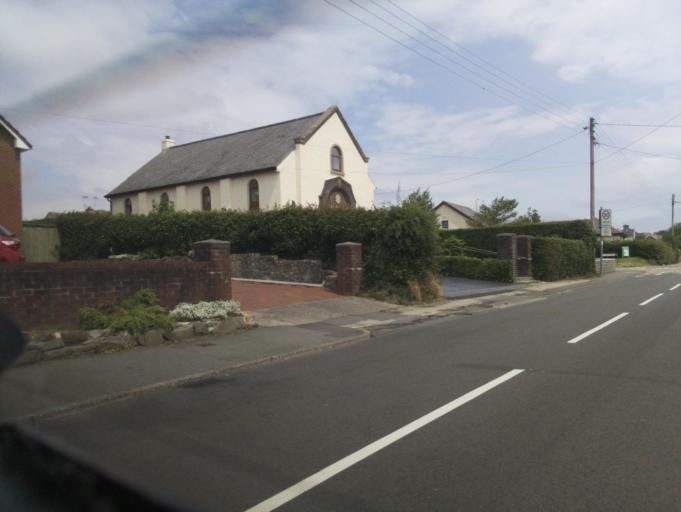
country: GB
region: Wales
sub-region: Vale of Glamorgan
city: Rhoose
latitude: 51.3883
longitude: -3.3547
